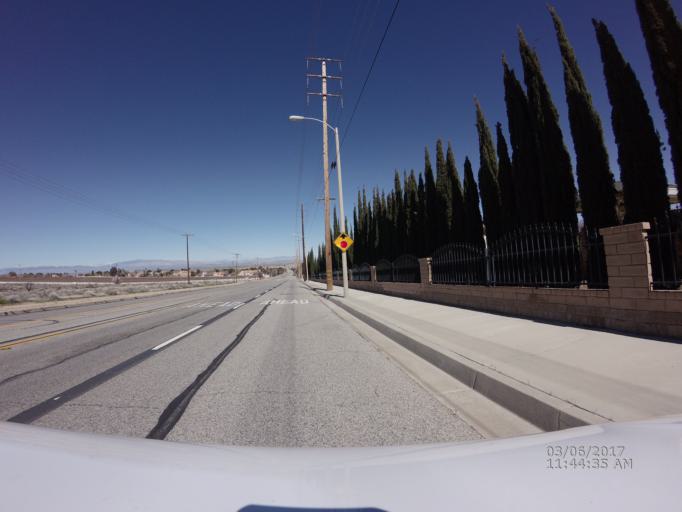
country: US
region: California
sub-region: Los Angeles County
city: Quartz Hill
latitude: 34.6368
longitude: -118.2361
